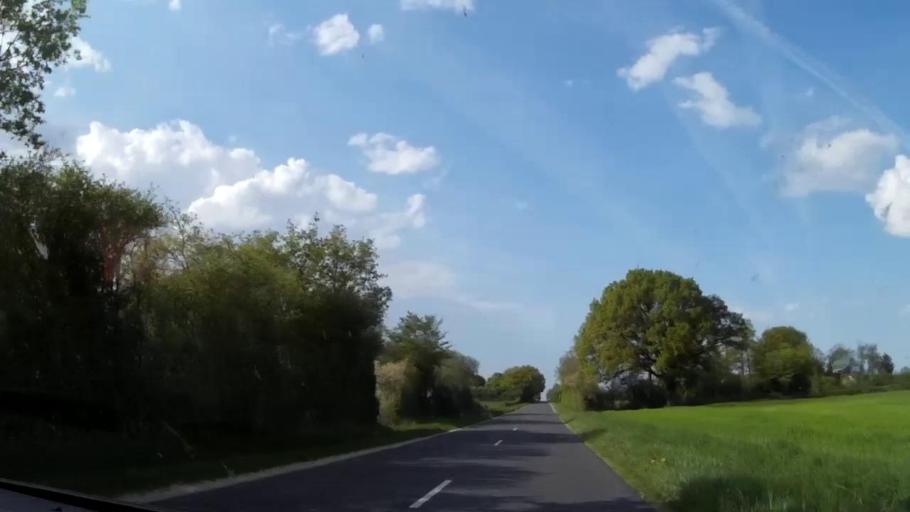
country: FR
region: Centre
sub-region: Departement du Loir-et-Cher
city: Mondoubleau
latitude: 47.9386
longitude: 0.9332
